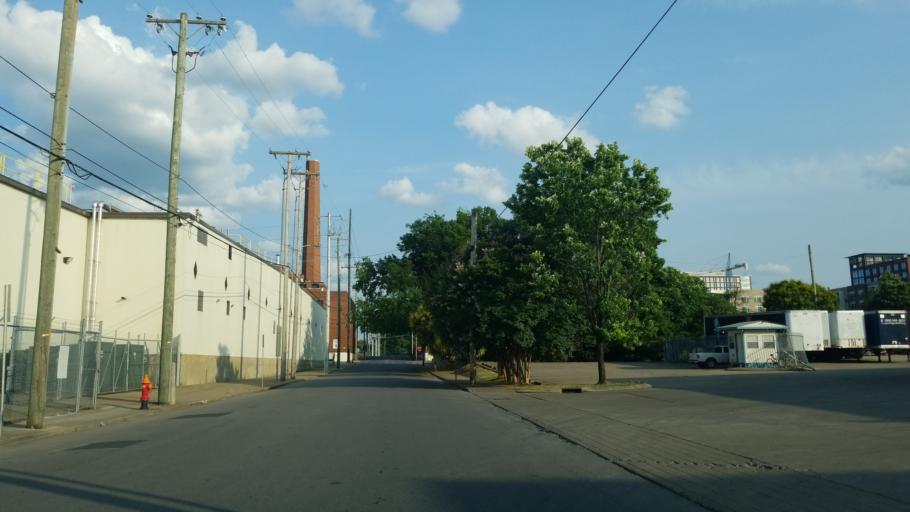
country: US
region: Tennessee
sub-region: Davidson County
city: Nashville
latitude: 36.1684
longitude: -86.7921
